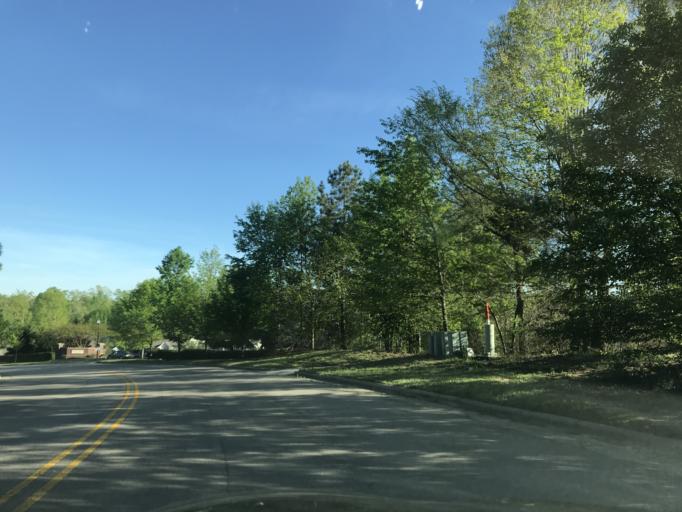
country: US
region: North Carolina
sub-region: Wake County
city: Raleigh
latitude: 35.8397
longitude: -78.5657
